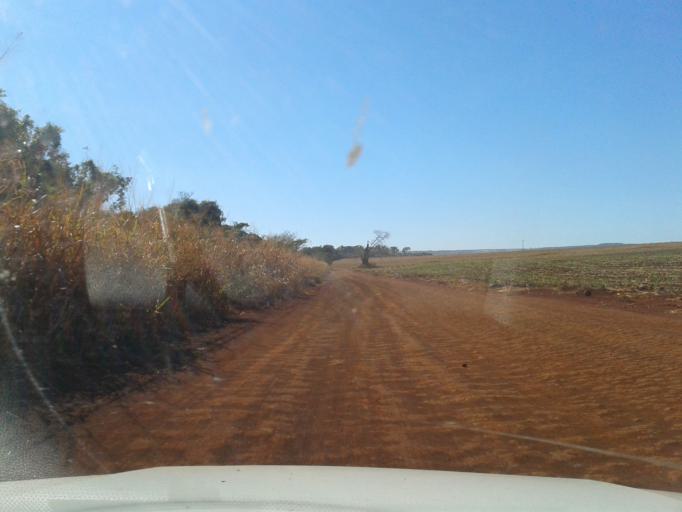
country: BR
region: Minas Gerais
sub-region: Centralina
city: Centralina
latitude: -18.5899
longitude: -49.1565
